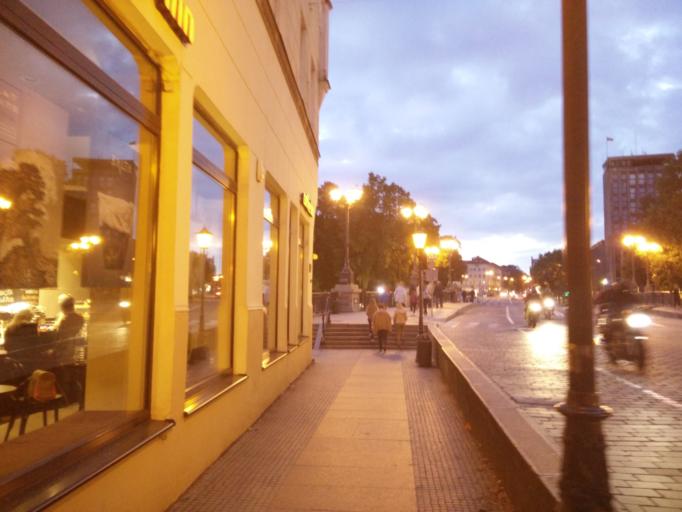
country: LT
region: Klaipedos apskritis
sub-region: Klaipeda
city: Klaipeda
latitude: 55.7097
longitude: 21.1338
